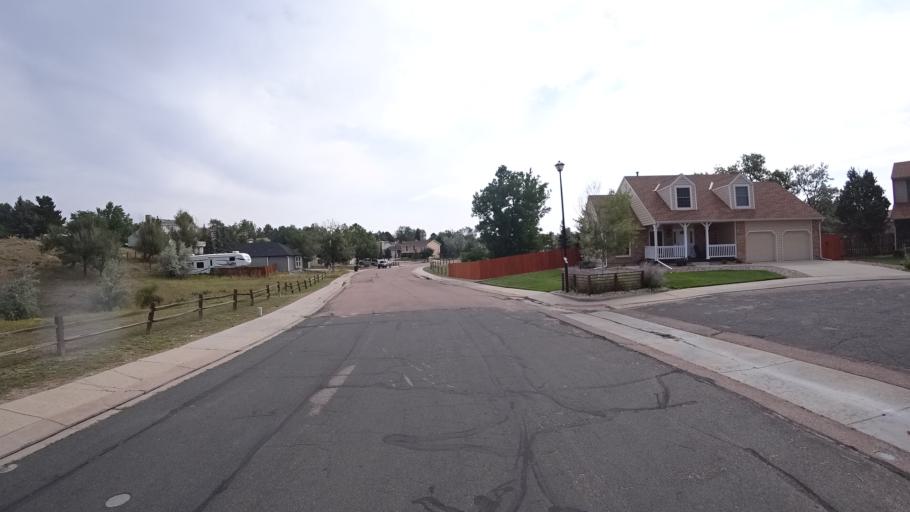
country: US
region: Colorado
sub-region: El Paso County
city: Air Force Academy
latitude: 38.9225
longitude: -104.8374
